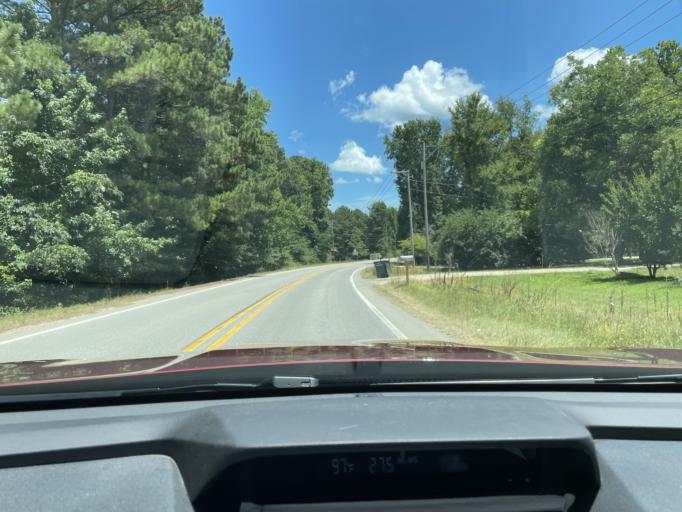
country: US
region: Arkansas
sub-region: Drew County
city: Monticello
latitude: 33.6285
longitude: -91.7572
